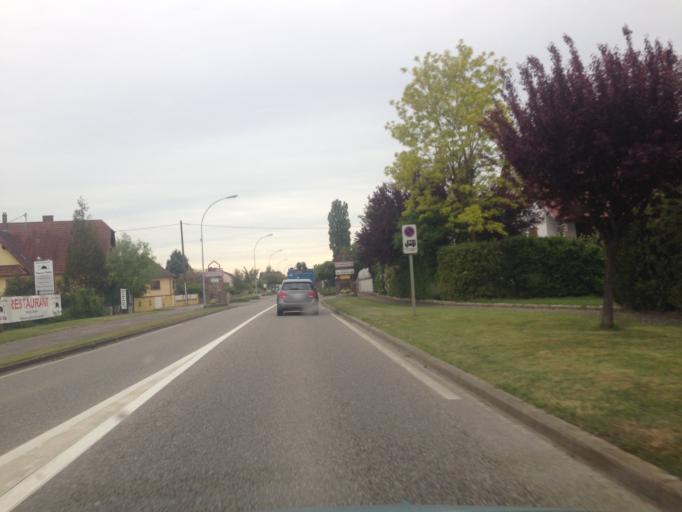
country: FR
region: Alsace
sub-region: Departement du Bas-Rhin
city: Mommenheim
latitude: 48.7546
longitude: 7.6554
